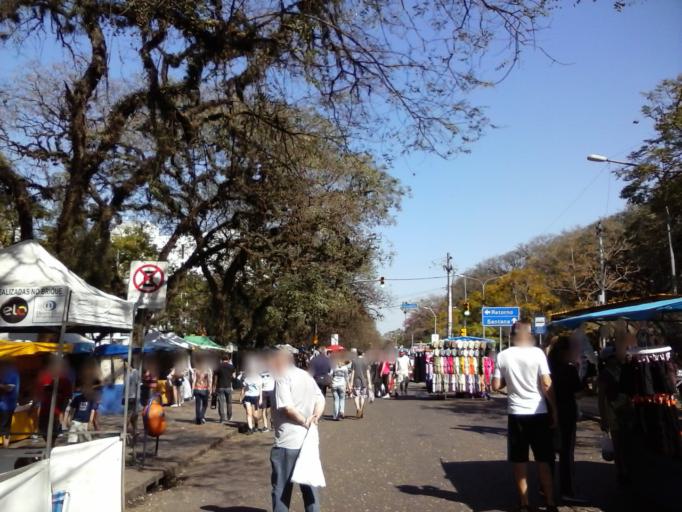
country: BR
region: Rio Grande do Sul
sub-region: Porto Alegre
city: Porto Alegre
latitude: -30.0368
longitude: -51.2112
